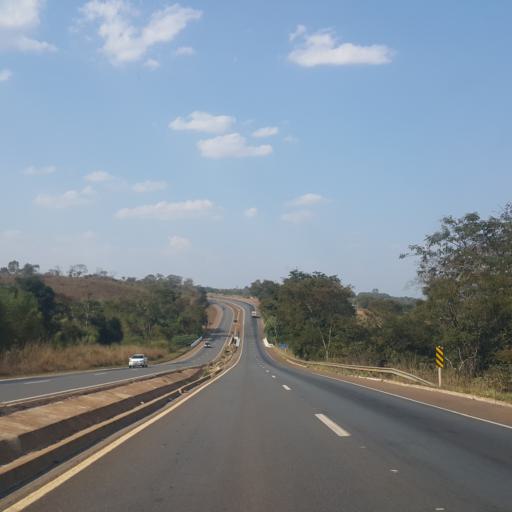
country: BR
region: Goias
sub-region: Abadiania
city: Abadiania
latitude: -16.2982
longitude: -48.8068
